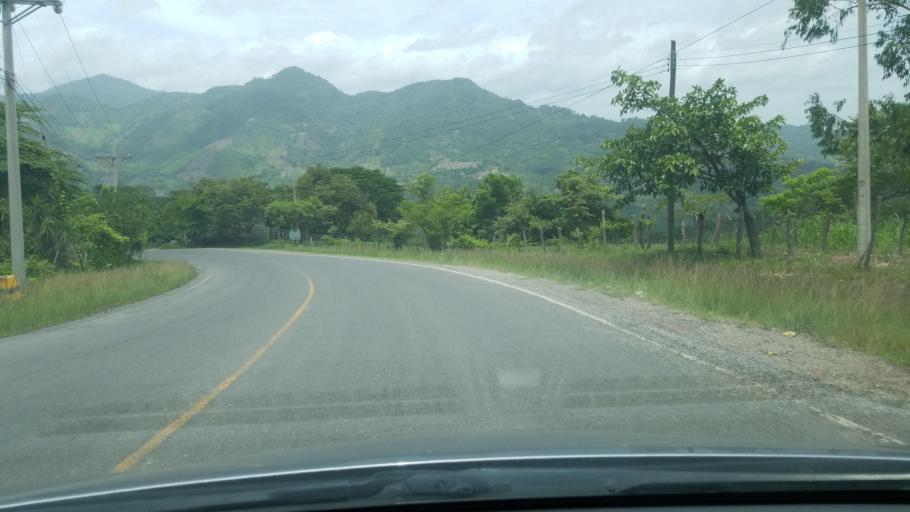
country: HN
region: Copan
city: Santa Rosa de Copan
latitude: 14.7274
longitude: -88.7675
